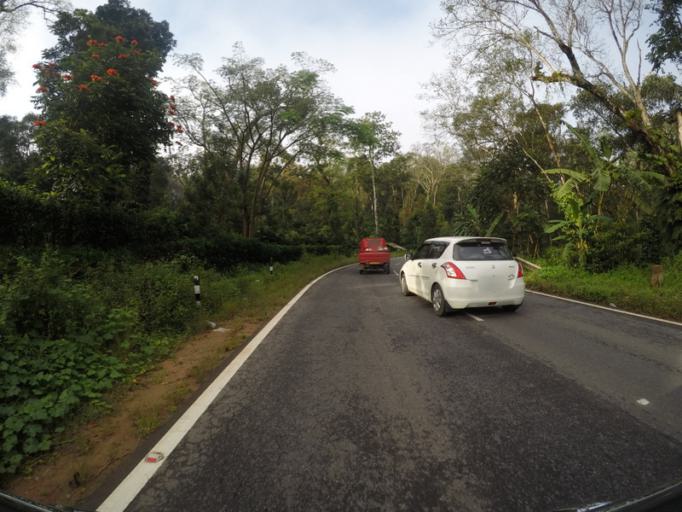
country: IN
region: Karnataka
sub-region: Kodagu
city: Suntikoppa
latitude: 12.4363
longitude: 75.8053
